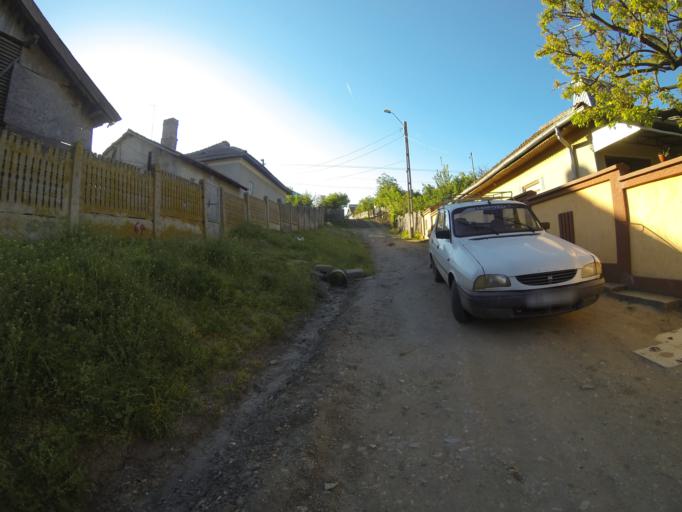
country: RO
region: Dolj
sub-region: Comuna Segarcea
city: Segarcea
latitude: 44.0968
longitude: 23.7403
